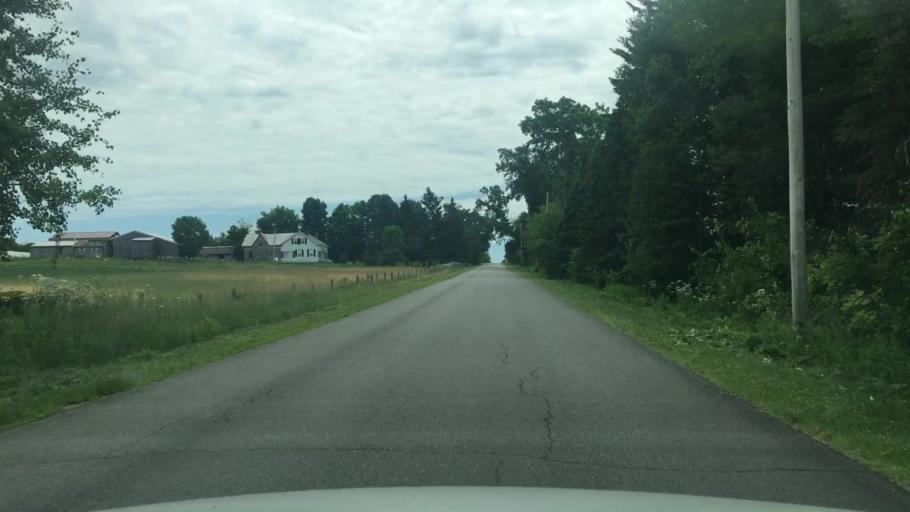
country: US
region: Maine
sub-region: Kennebec County
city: Albion
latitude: 44.4789
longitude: -69.3694
